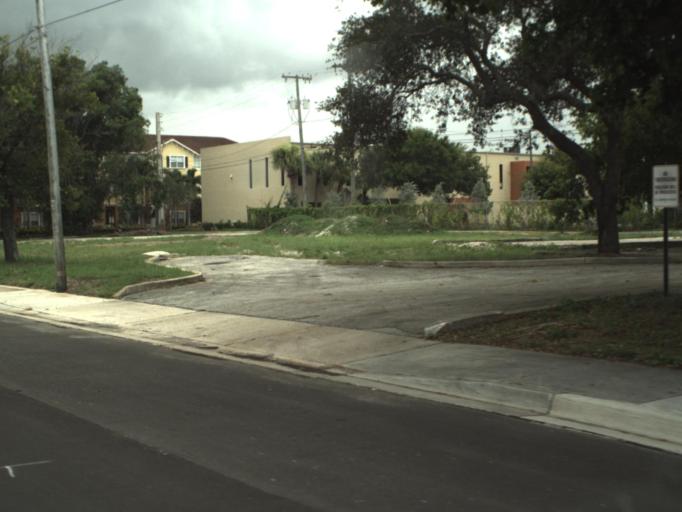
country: US
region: Florida
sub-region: Palm Beach County
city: Delray Beach
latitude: 26.4681
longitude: -80.0682
